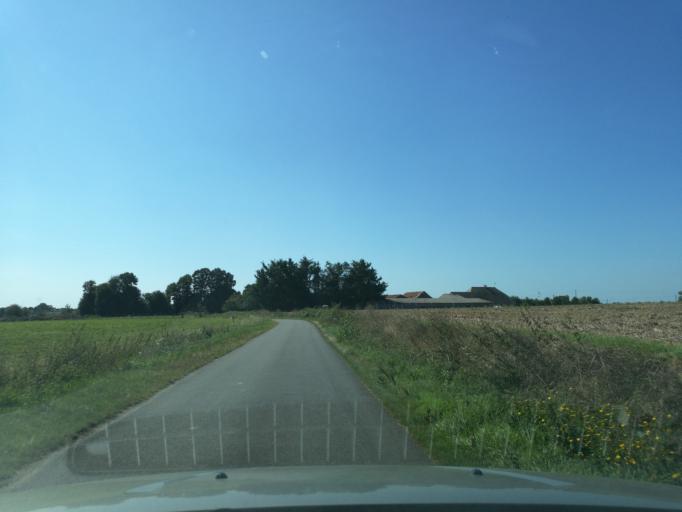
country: FR
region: Brittany
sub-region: Departement d'Ille-et-Vilaine
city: Bedee
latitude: 48.1912
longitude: -1.9536
